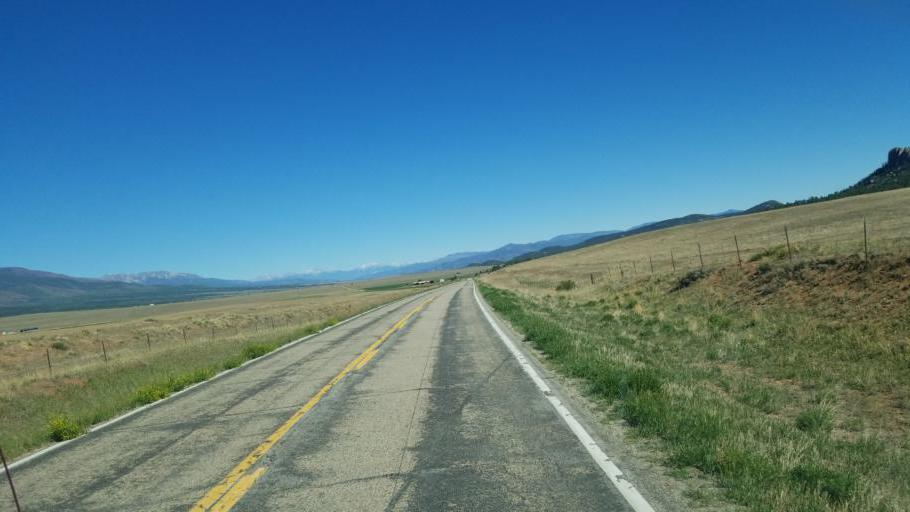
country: US
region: Colorado
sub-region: Custer County
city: Westcliffe
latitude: 38.2049
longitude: -105.5393
